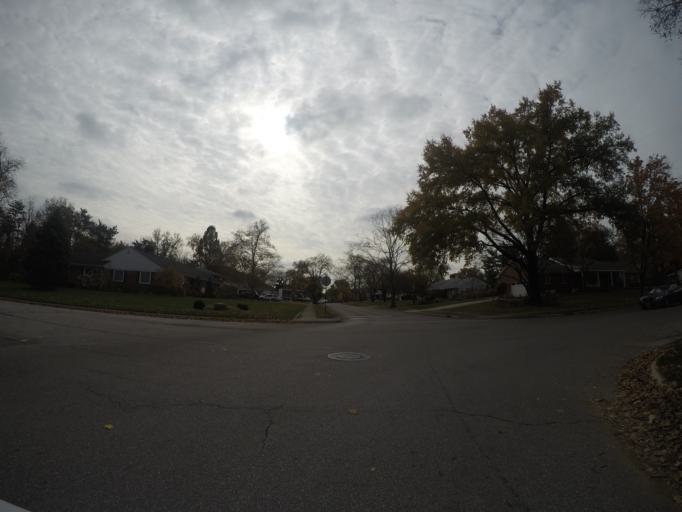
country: US
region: Ohio
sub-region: Franklin County
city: Upper Arlington
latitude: 40.0191
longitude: -83.0478
